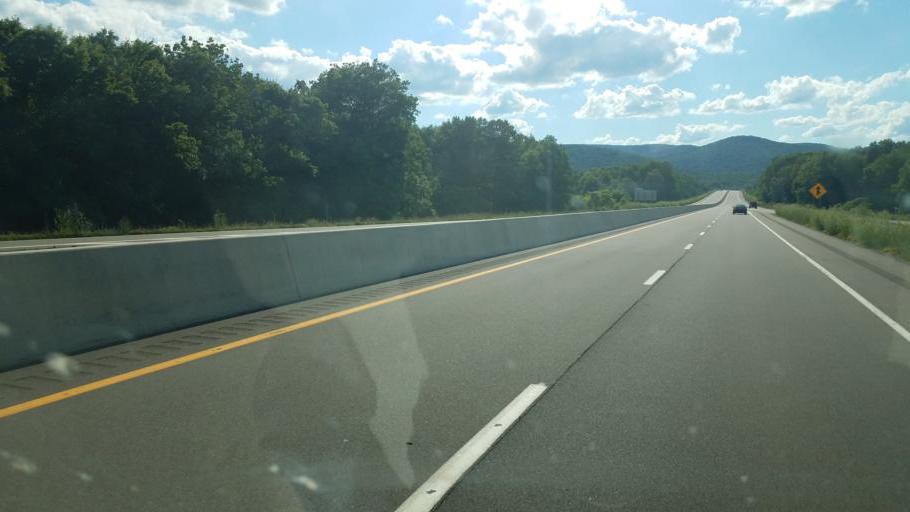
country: US
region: New York
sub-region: Cattaraugus County
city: Salamanca
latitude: 42.0888
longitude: -78.6333
